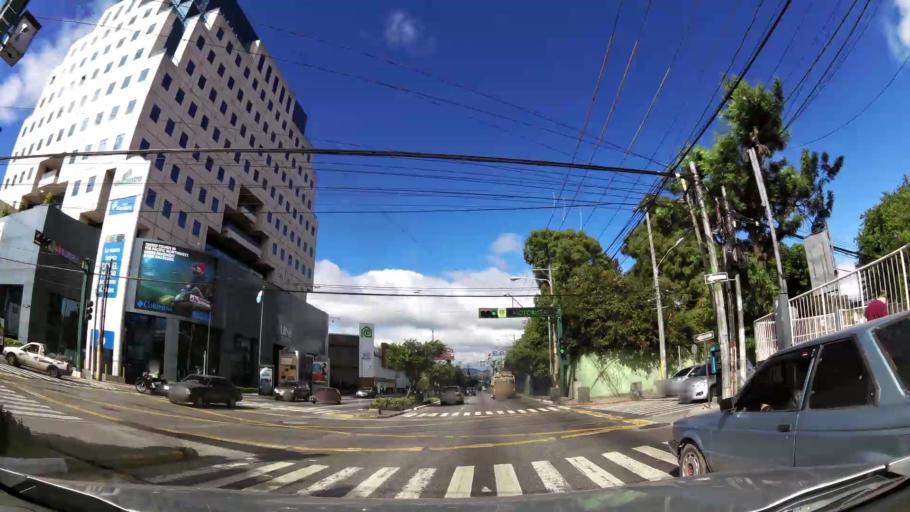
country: GT
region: Guatemala
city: Santa Catarina Pinula
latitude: 14.5926
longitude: -90.5117
